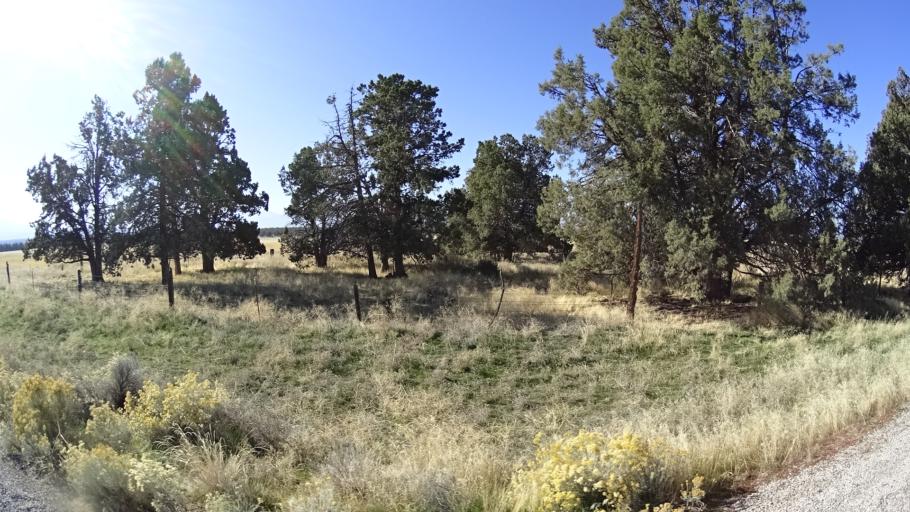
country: US
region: California
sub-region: Siskiyou County
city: Weed
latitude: 41.6202
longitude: -122.3227
